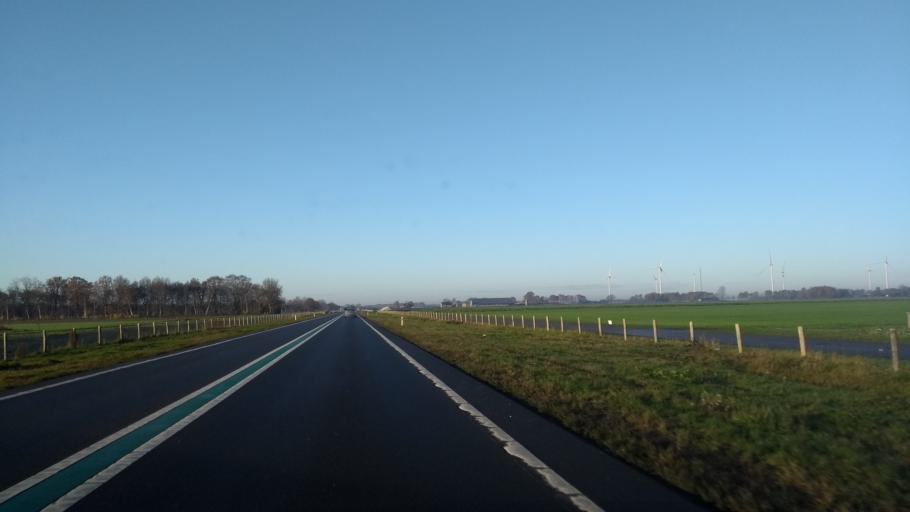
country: NL
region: Overijssel
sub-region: Gemeente Twenterand
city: Magele
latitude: 52.5590
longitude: 6.4983
